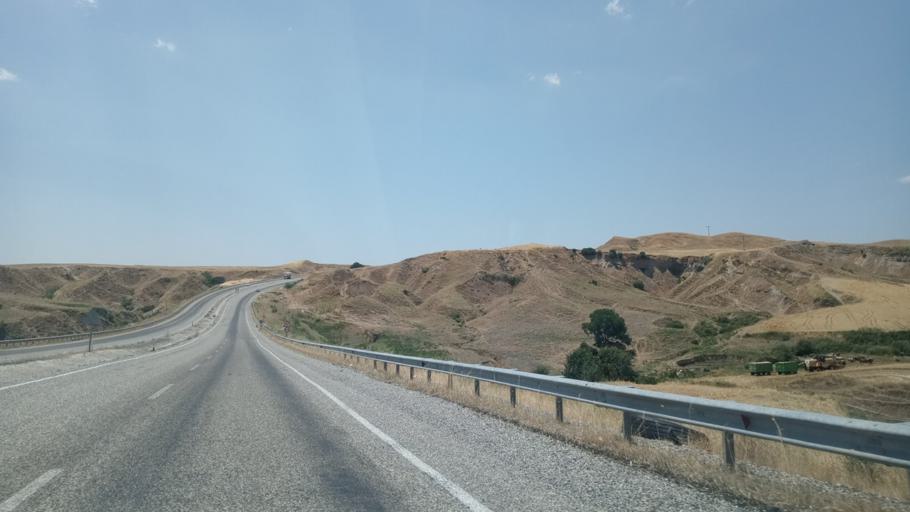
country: TR
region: Batman
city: Bekirhan
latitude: 38.1400
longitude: 41.2766
